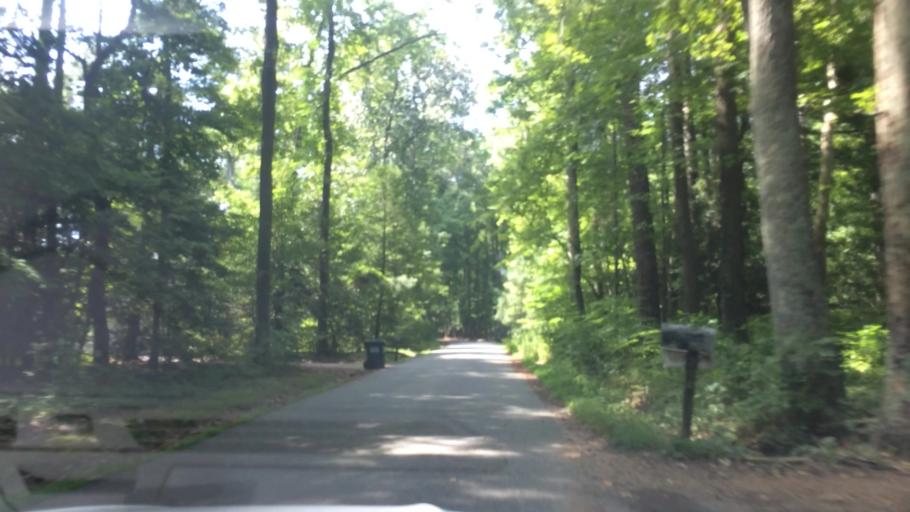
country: US
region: Virginia
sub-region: City of Poquoson
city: Poquoson
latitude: 37.1605
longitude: -76.4266
